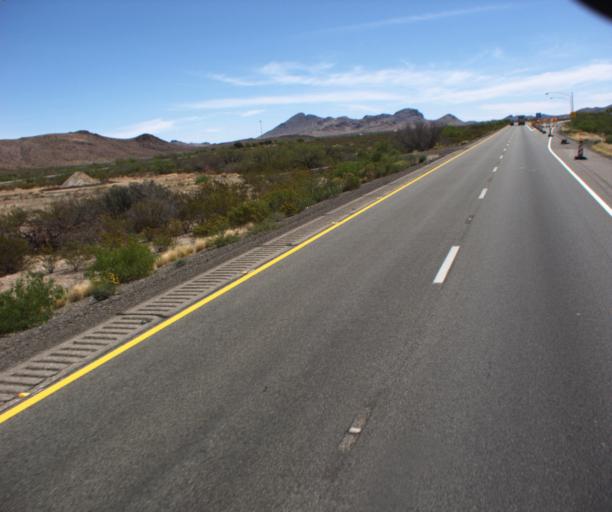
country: US
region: New Mexico
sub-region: Hidalgo County
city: Lordsburg
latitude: 32.2380
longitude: -109.0950
